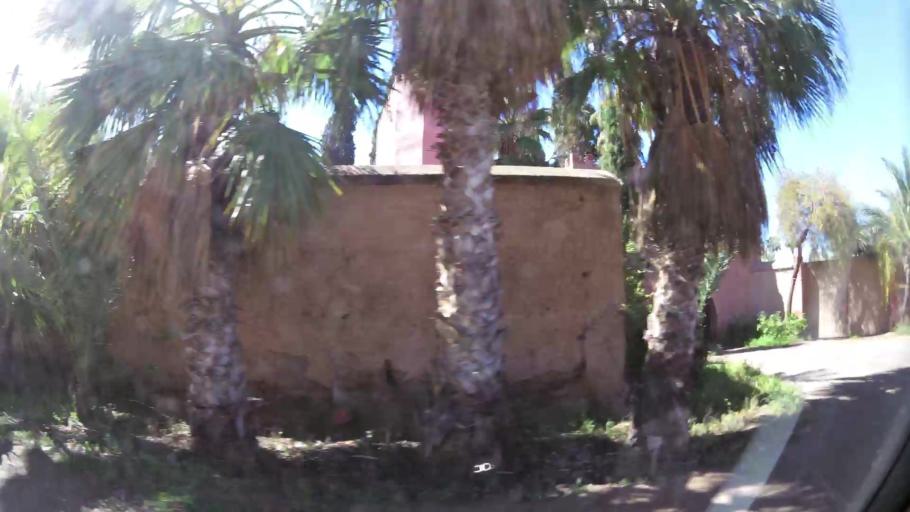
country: MA
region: Marrakech-Tensift-Al Haouz
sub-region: Marrakech
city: Marrakesh
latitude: 31.6654
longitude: -7.9587
